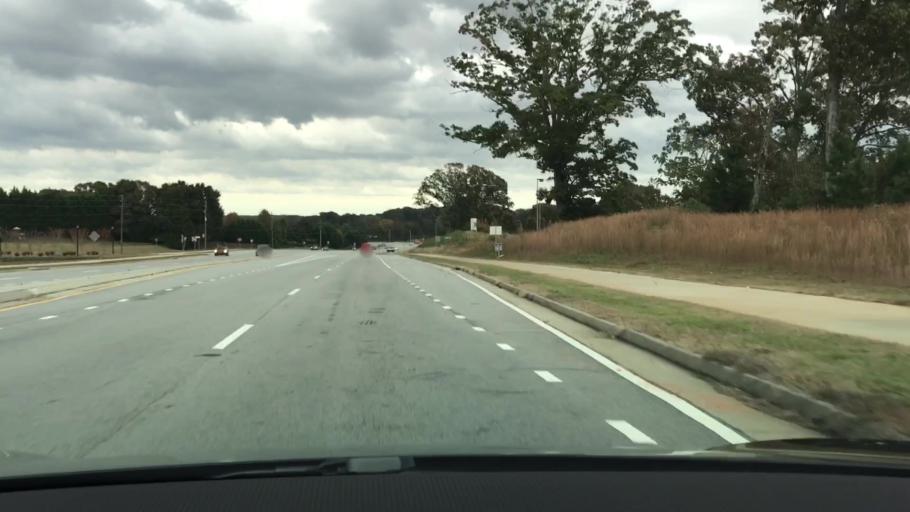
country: US
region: Georgia
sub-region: Jackson County
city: Braselton
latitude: 34.1138
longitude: -83.8517
